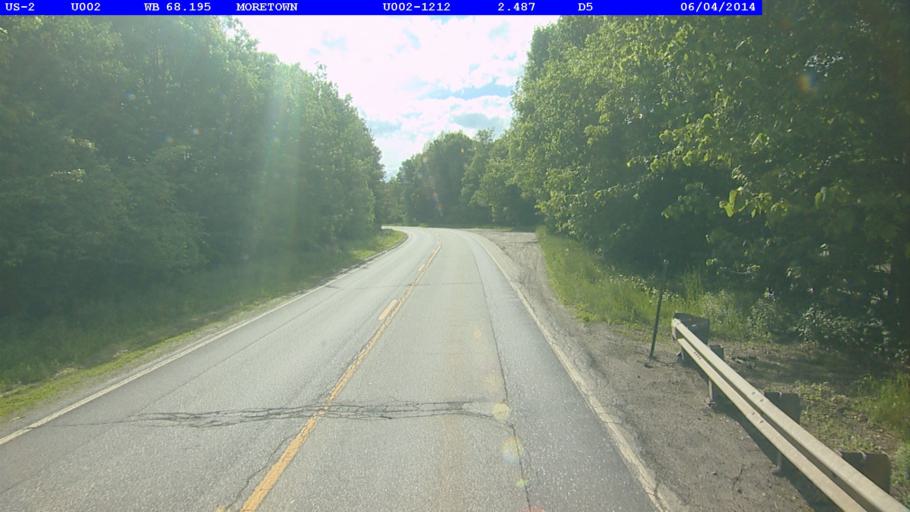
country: US
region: Vermont
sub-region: Washington County
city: Waterbury
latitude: 44.3133
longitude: -72.7055
